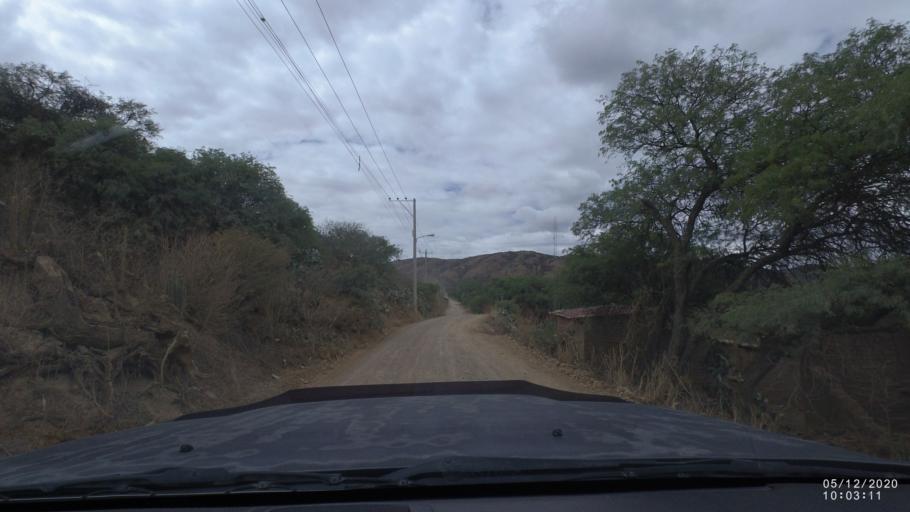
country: BO
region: Cochabamba
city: Sipe Sipe
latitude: -17.4556
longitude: -66.2866
